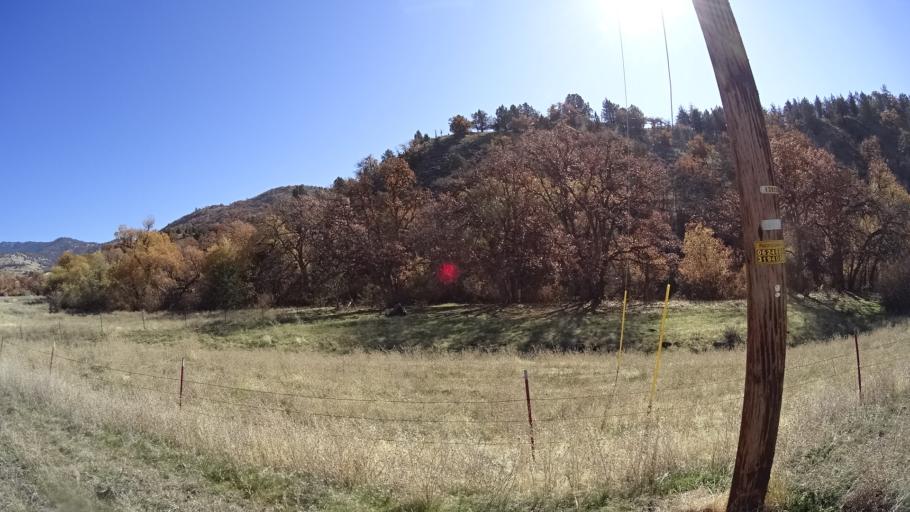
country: US
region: California
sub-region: Siskiyou County
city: Montague
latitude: 41.7932
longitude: -122.3427
